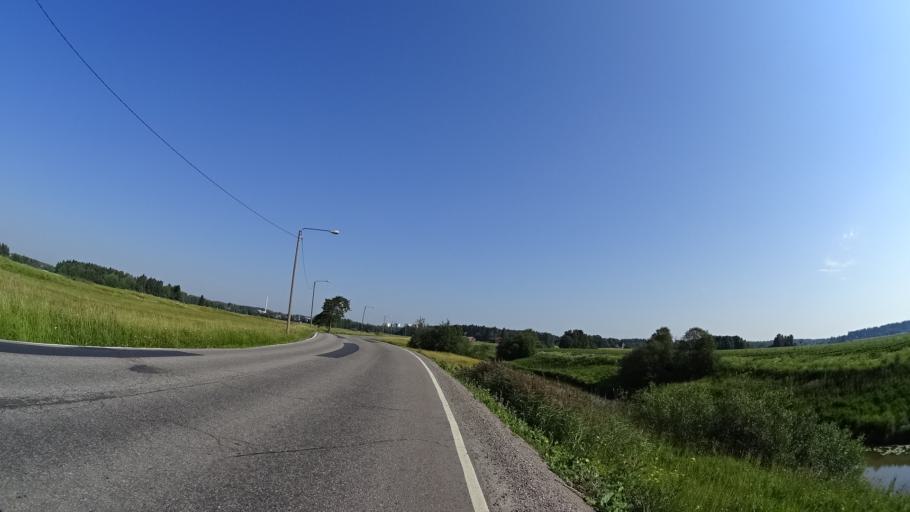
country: FI
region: Uusimaa
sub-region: Helsinki
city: Vantaa
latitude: 60.3062
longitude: 25.0688
